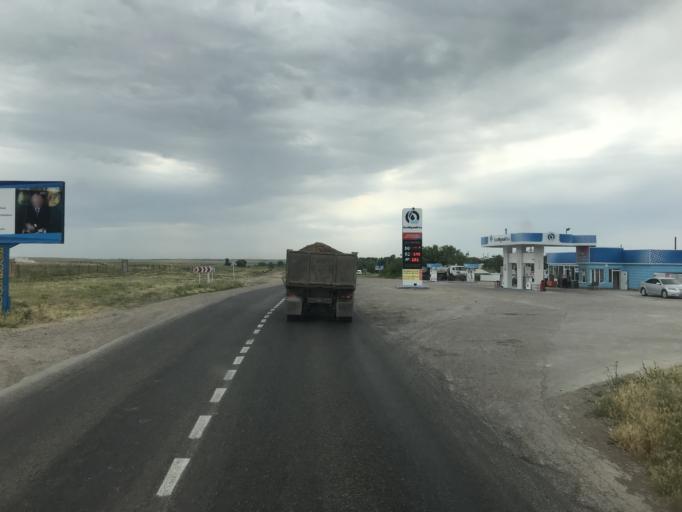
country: KZ
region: Ongtustik Qazaqstan
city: Saryaghash
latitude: 41.3962
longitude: 69.0399
